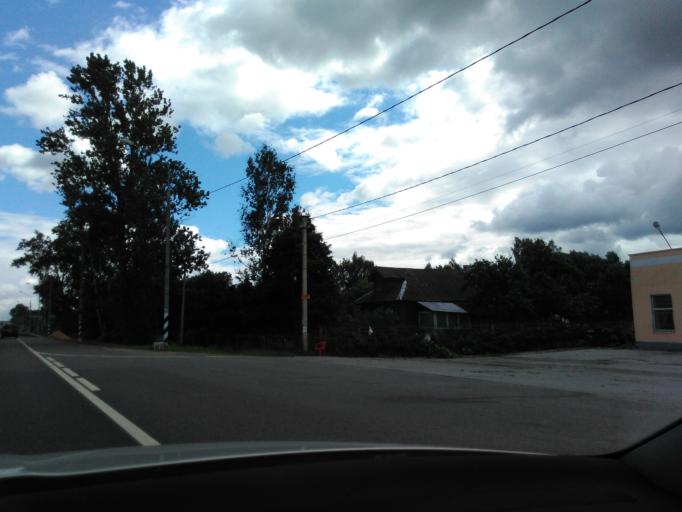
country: RU
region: Moskovskaya
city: Klin
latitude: 56.2859
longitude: 36.8184
